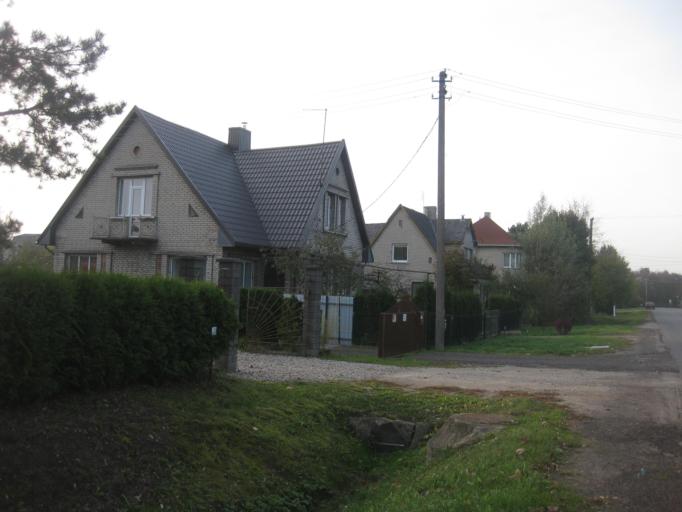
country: LT
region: Kauno apskritis
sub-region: Kaunas
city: Kaunas
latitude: 54.8917
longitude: 23.8740
